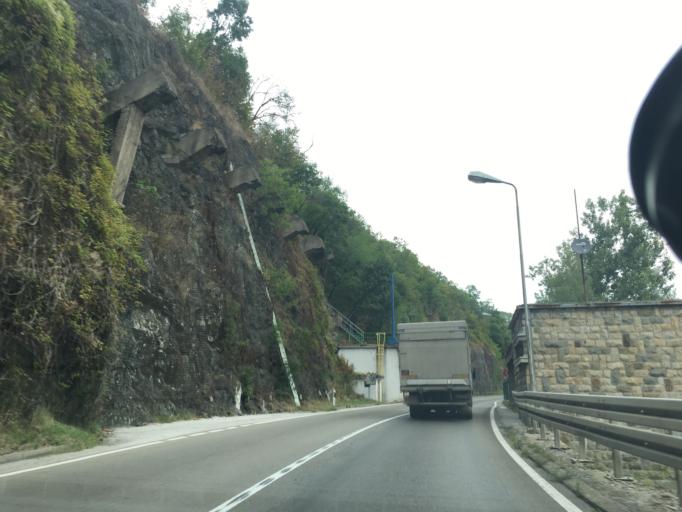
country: RS
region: Central Serbia
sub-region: Moravicki Okrug
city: Lucani
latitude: 43.9087
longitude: 20.2316
